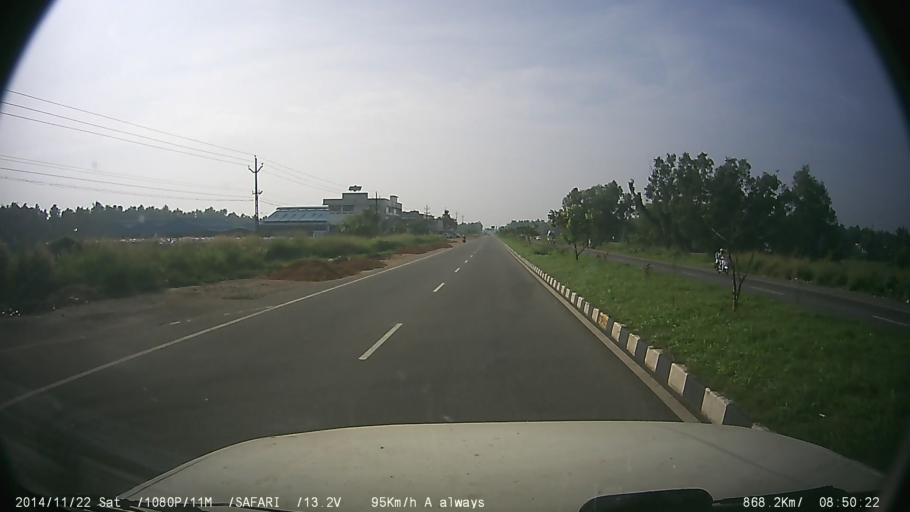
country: IN
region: Kerala
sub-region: Thrissur District
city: Trichur
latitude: 10.4624
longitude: 76.2579
